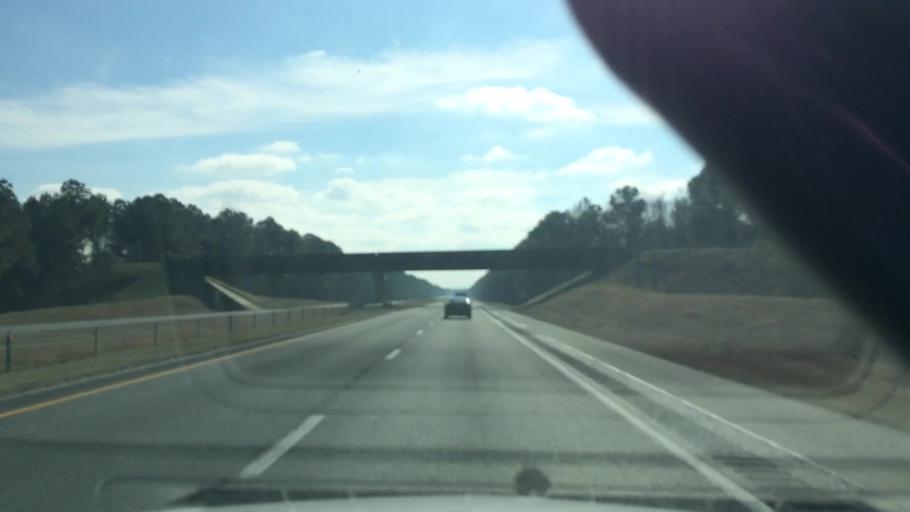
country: US
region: North Carolina
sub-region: Duplin County
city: Wallace
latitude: 34.7330
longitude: -77.9449
